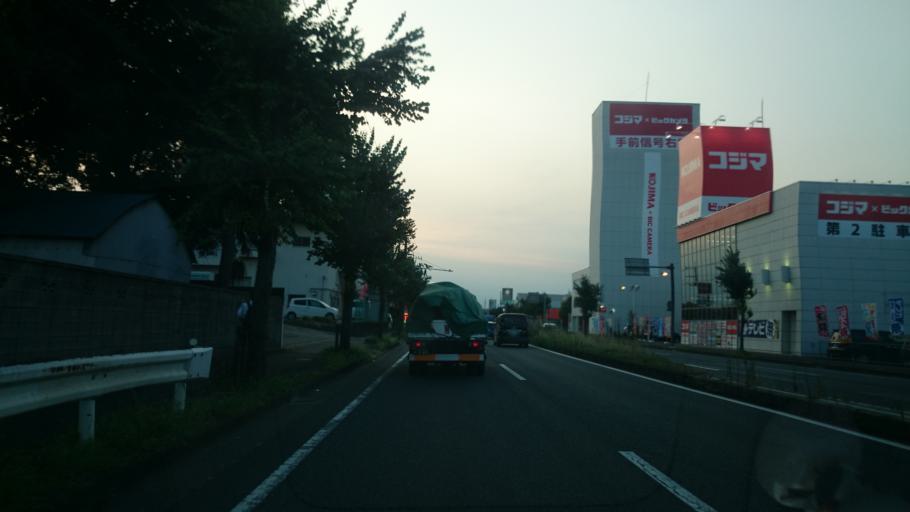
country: JP
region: Saitama
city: Iwatsuki
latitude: 35.9510
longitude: 139.6680
